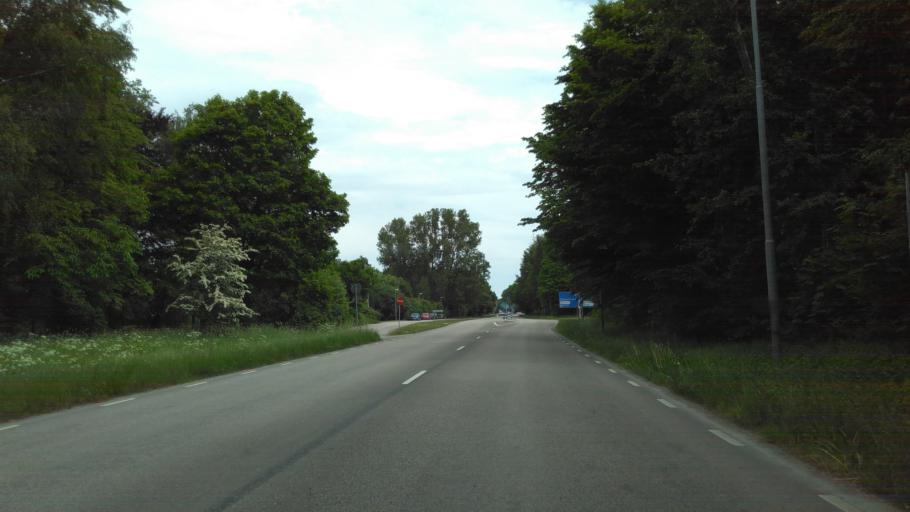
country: SE
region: Vaestra Goetaland
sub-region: Lidkopings Kommun
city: Lidkoping
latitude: 58.4882
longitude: 13.1411
